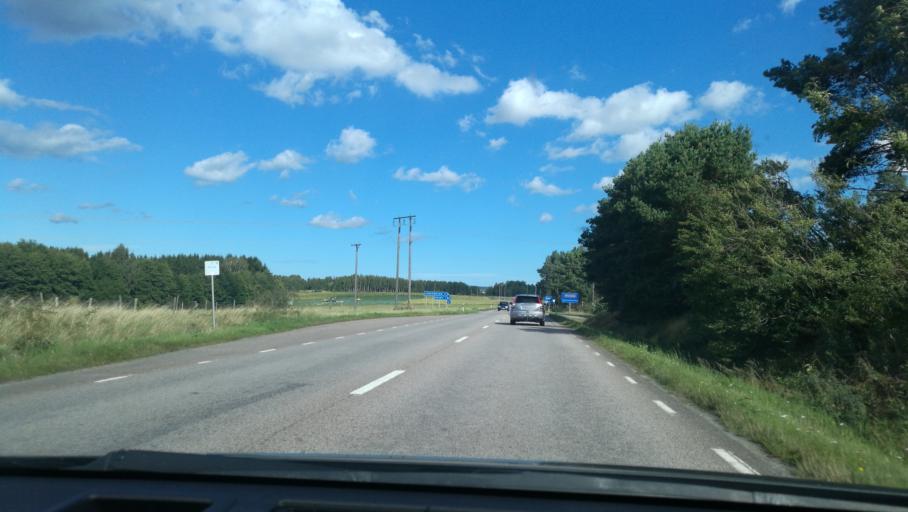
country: SE
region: Vaestra Goetaland
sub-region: Gotene Kommun
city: Kallby
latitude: 58.4961
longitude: 13.2981
